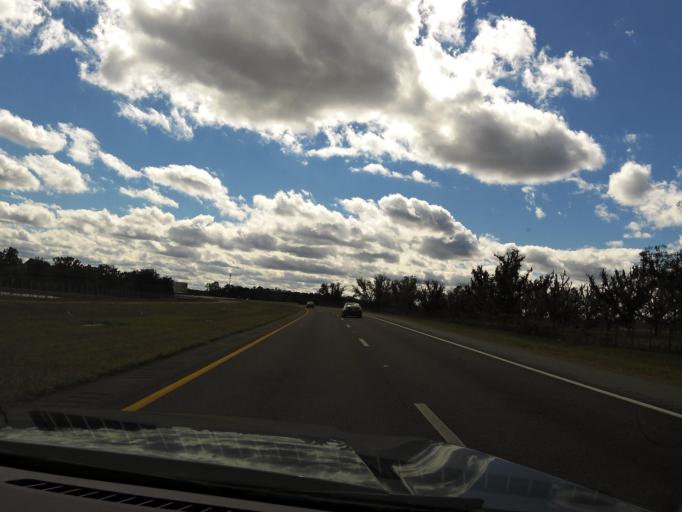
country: US
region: Florida
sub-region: Bradford County
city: Starke
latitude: 29.9286
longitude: -82.1379
